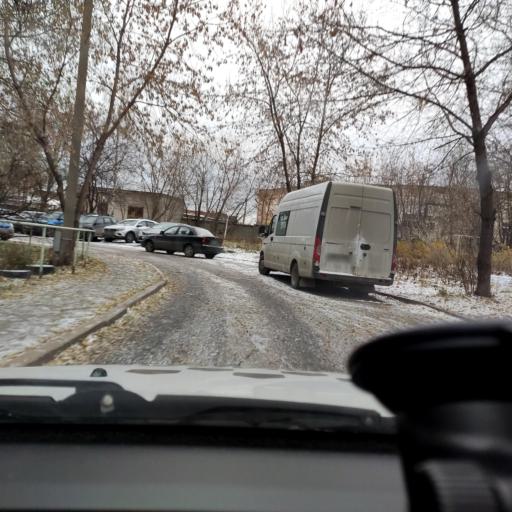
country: RU
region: Perm
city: Perm
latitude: 58.0225
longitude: 56.2730
